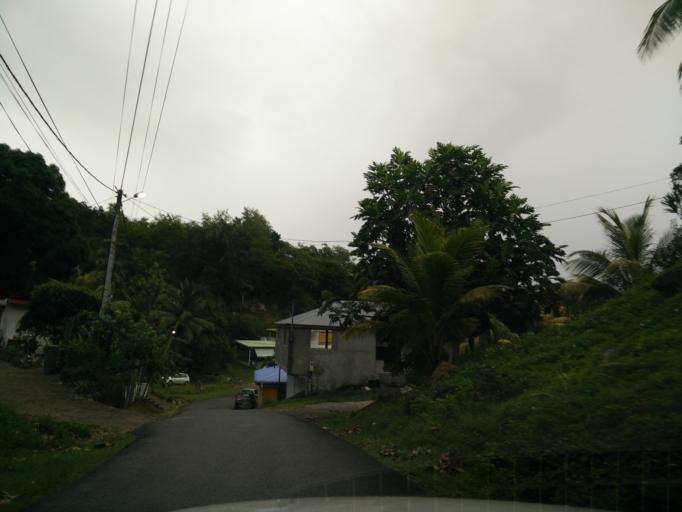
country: GP
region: Guadeloupe
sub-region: Guadeloupe
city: Le Gosier
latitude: 16.2348
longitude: -61.4928
